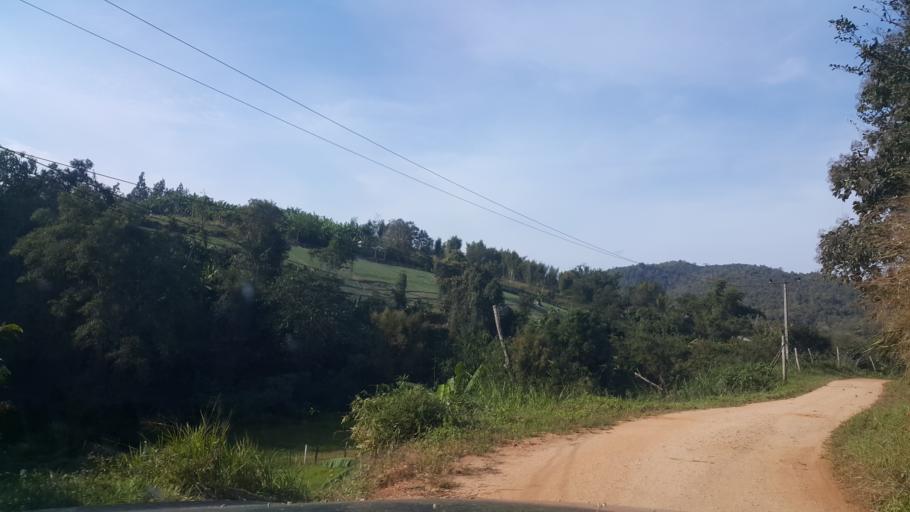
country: TH
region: Chiang Mai
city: Samoeng
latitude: 18.9531
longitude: 98.6752
